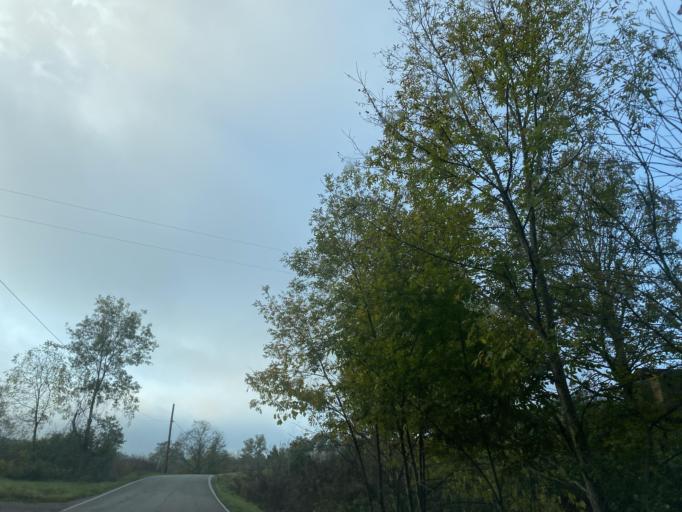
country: US
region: Kentucky
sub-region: Pendleton County
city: Falmouth
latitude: 38.7403
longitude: -84.3167
